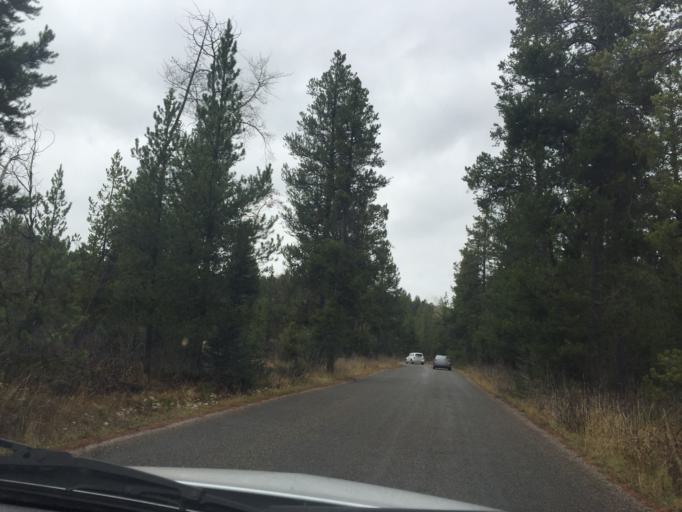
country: US
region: Wyoming
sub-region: Teton County
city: Moose Wilson Road
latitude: 43.6294
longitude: -110.7732
